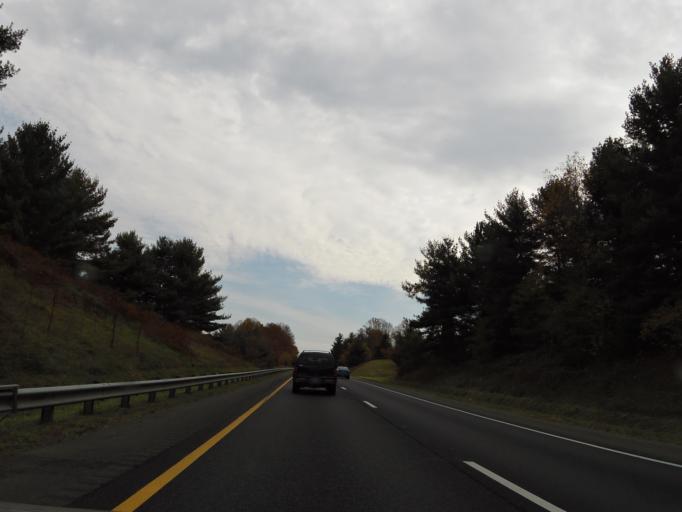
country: US
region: Virginia
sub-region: Carroll County
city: Woodlawn
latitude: 36.7714
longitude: -80.8093
